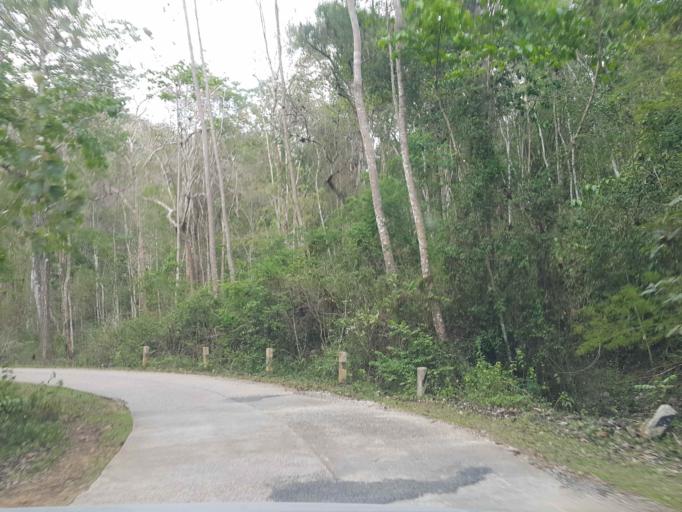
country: TH
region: Chiang Mai
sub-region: Amphoe Chiang Dao
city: Chiang Dao
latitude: 19.3763
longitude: 98.7582
